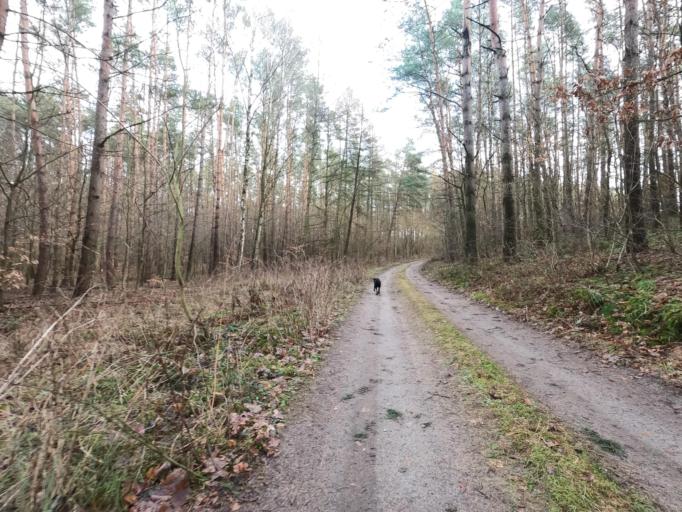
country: PL
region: Greater Poland Voivodeship
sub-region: Powiat pilski
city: Miasteczko Krajenskie
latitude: 53.1159
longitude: 16.9868
